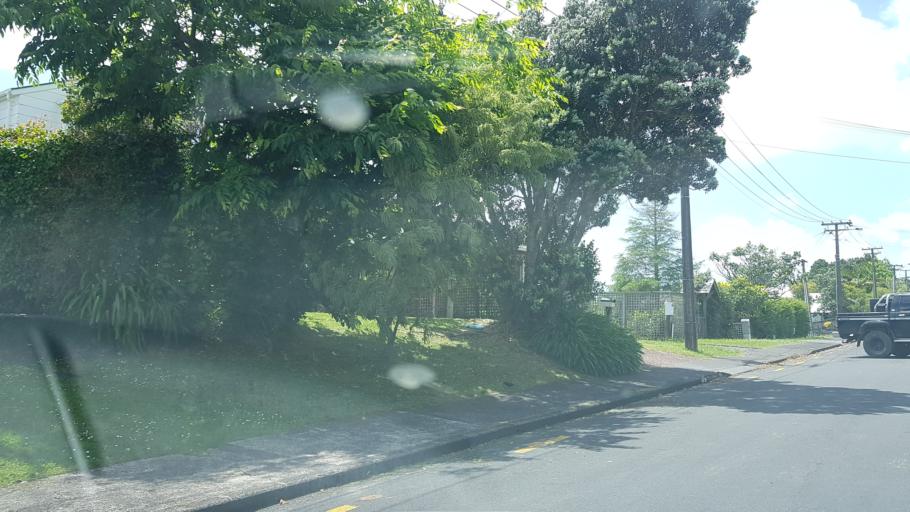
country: NZ
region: Auckland
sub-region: Auckland
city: North Shore
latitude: -36.7899
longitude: 174.6799
